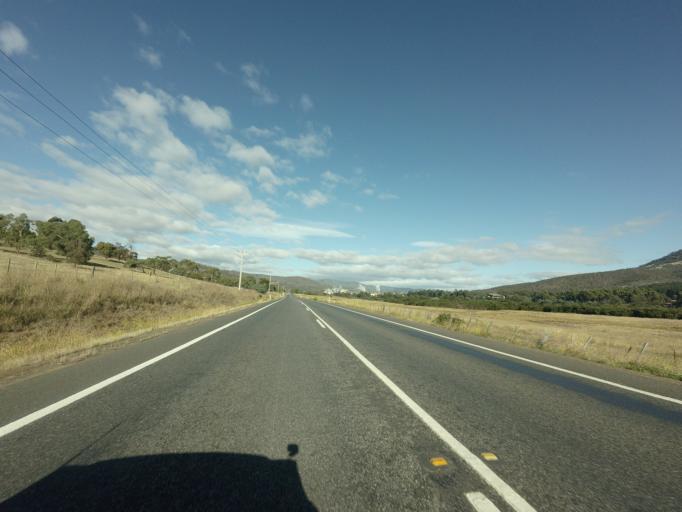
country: AU
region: Tasmania
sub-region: Derwent Valley
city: New Norfolk
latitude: -42.7747
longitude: 147.1199
